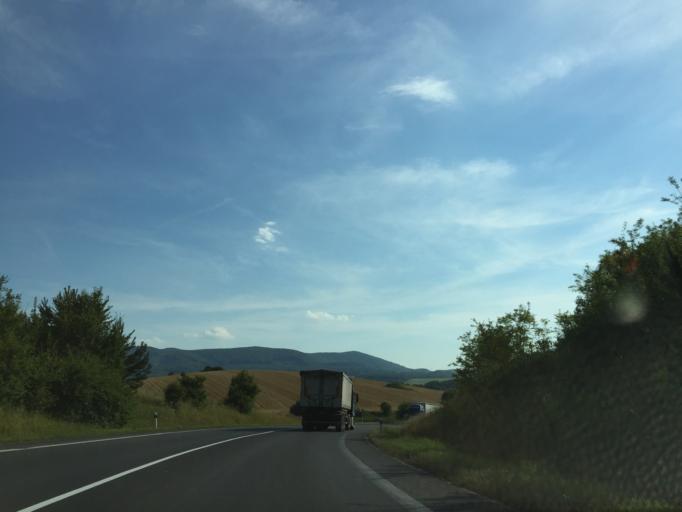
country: SK
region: Presovsky
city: Giraltovce
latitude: 49.0492
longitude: 21.4234
